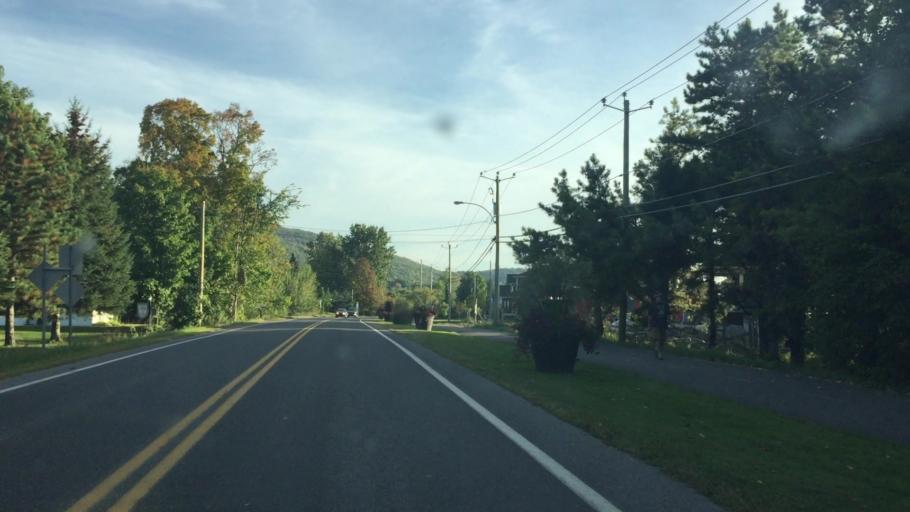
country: CA
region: Quebec
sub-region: Monteregie
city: Bromont
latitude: 45.3109
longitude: -72.6574
